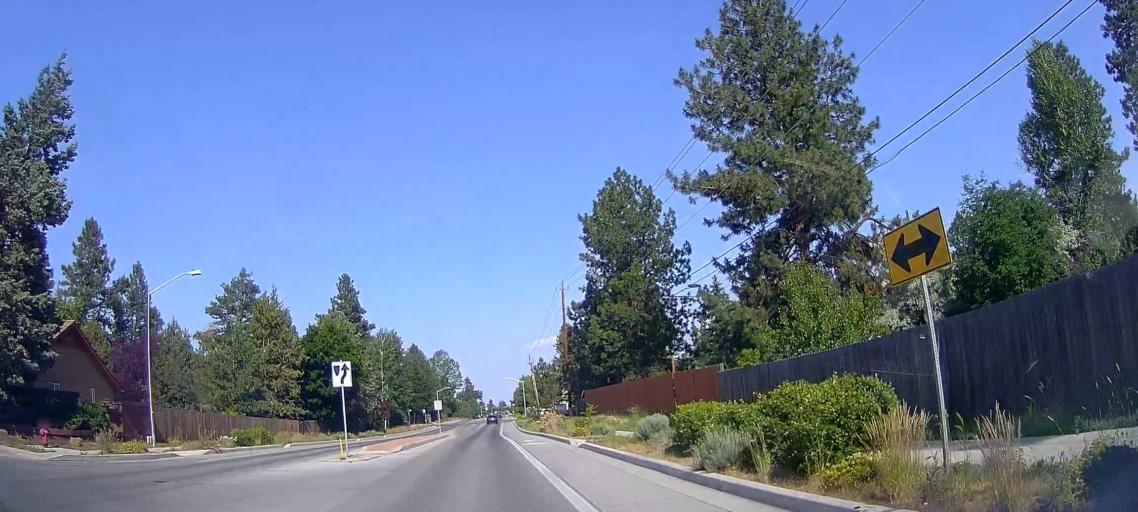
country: US
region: Oregon
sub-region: Deschutes County
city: Bend
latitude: 44.0371
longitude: -121.2743
